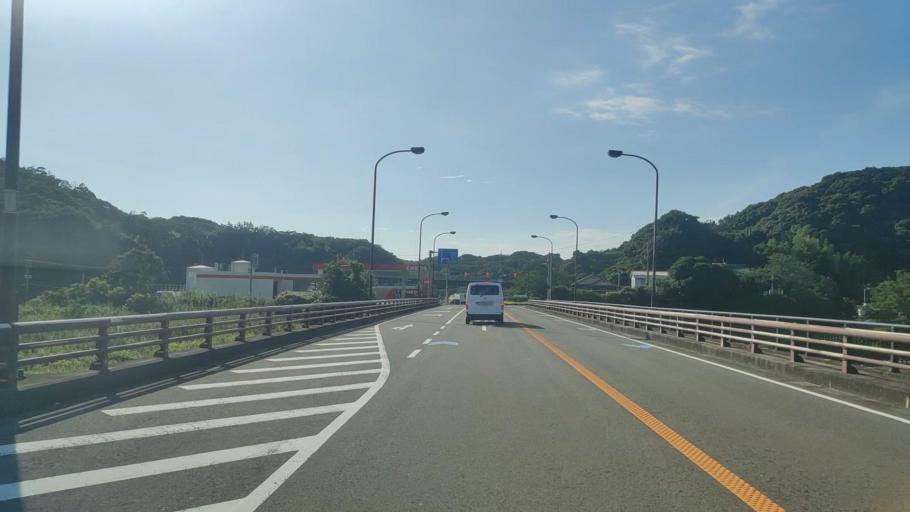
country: JP
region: Wakayama
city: Tanabe
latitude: 33.6800
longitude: 135.4080
